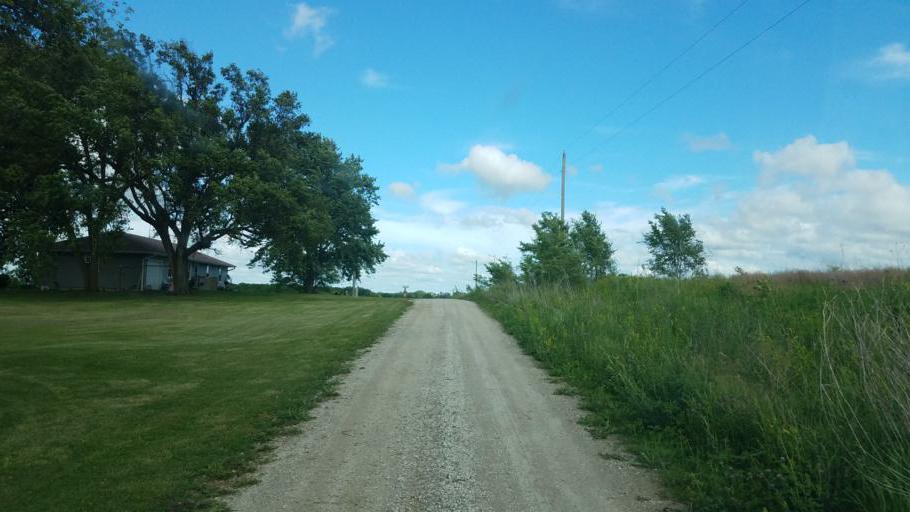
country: US
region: Missouri
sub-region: Mercer County
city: Princeton
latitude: 40.2601
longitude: -93.7015
